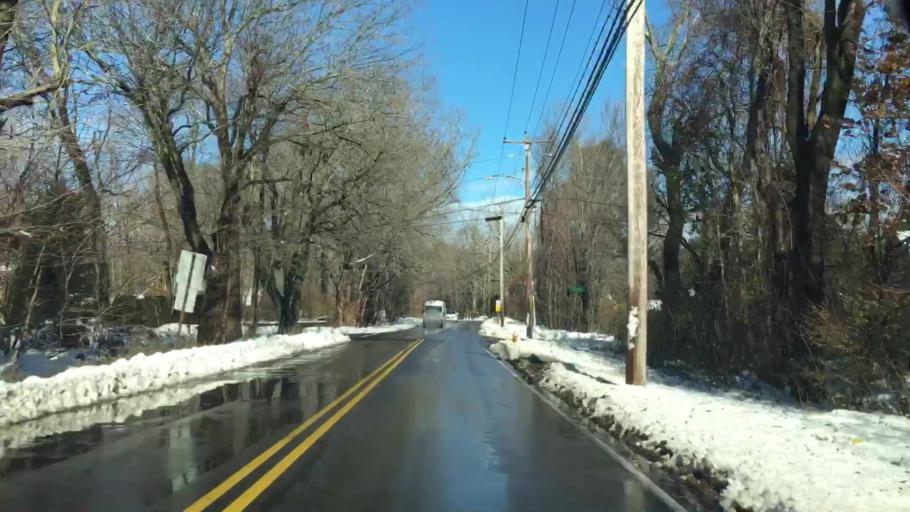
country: US
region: Connecticut
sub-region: Fairfield County
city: Trumbull
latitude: 41.3101
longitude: -73.1685
